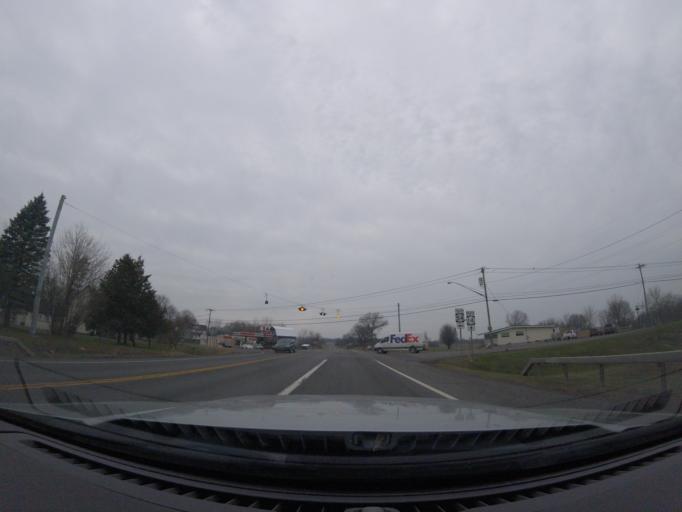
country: US
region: New York
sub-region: Yates County
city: Penn Yan
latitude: 42.6805
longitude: -76.9626
